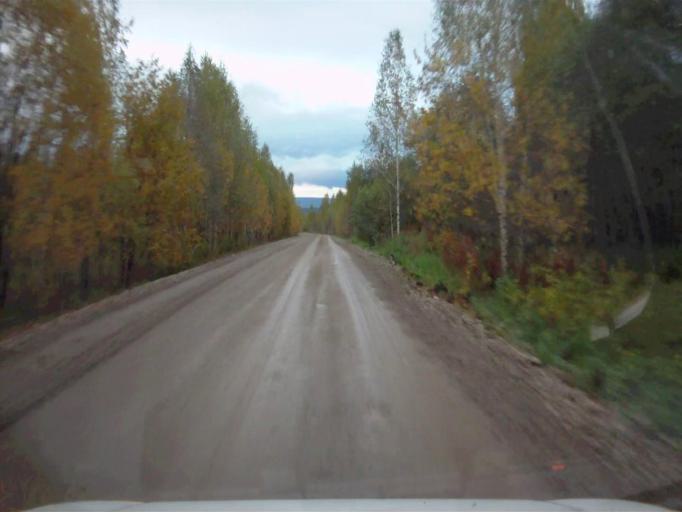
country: RU
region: Sverdlovsk
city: Mikhaylovsk
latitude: 56.1942
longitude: 59.1963
